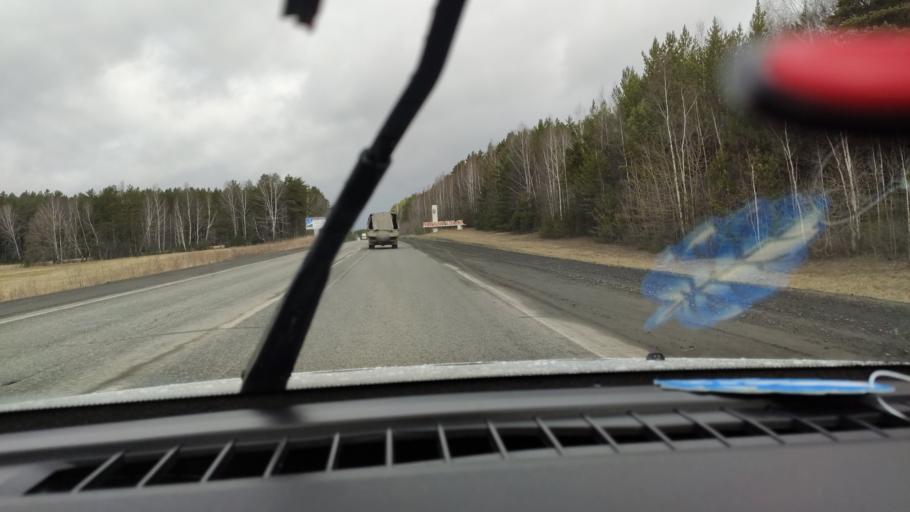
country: RU
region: Sverdlovsk
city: Talitsa
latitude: 56.8714
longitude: 60.0385
